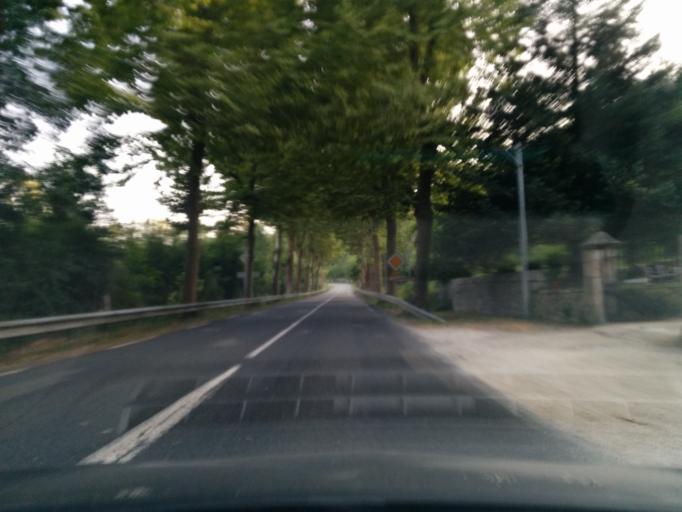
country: FR
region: Midi-Pyrenees
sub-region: Departement du Lot
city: Le Vigan
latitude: 44.6614
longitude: 1.4801
